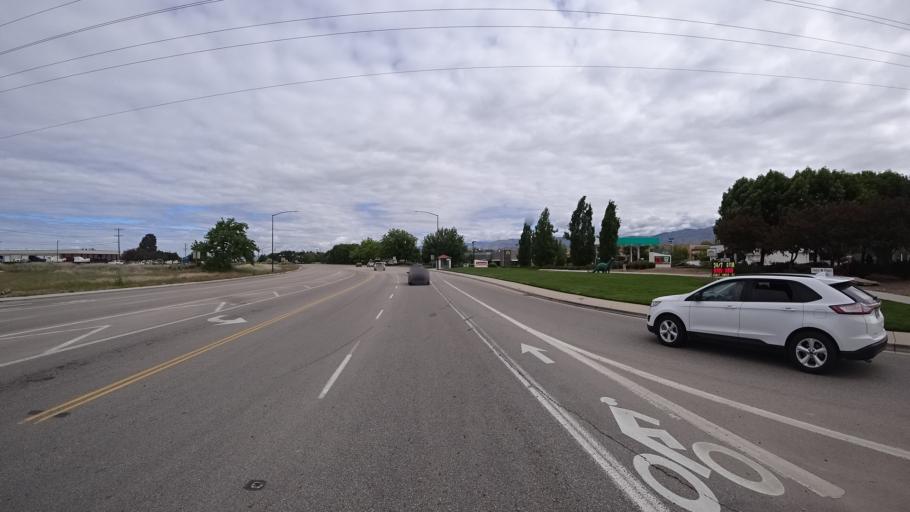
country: US
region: Idaho
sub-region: Ada County
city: Boise
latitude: 43.5412
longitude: -116.1553
